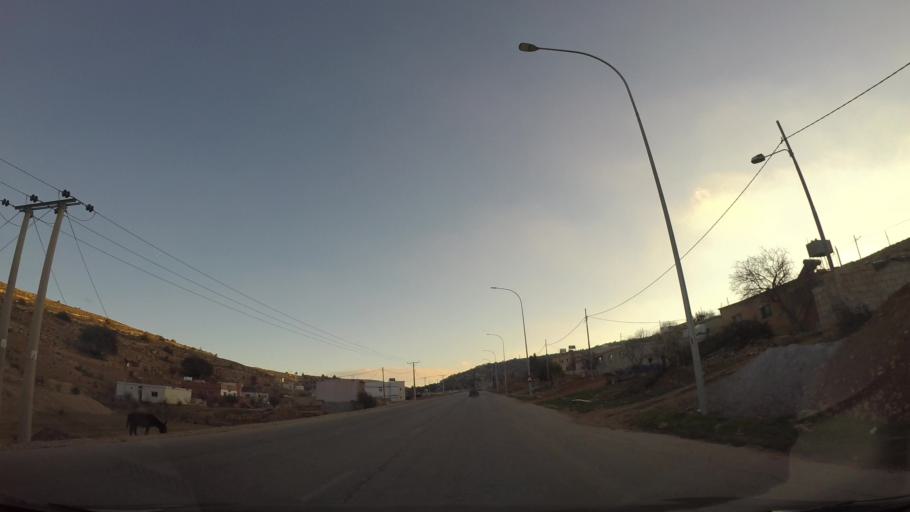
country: JO
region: Ma'an
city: Petra
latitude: 30.4191
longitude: 35.5104
